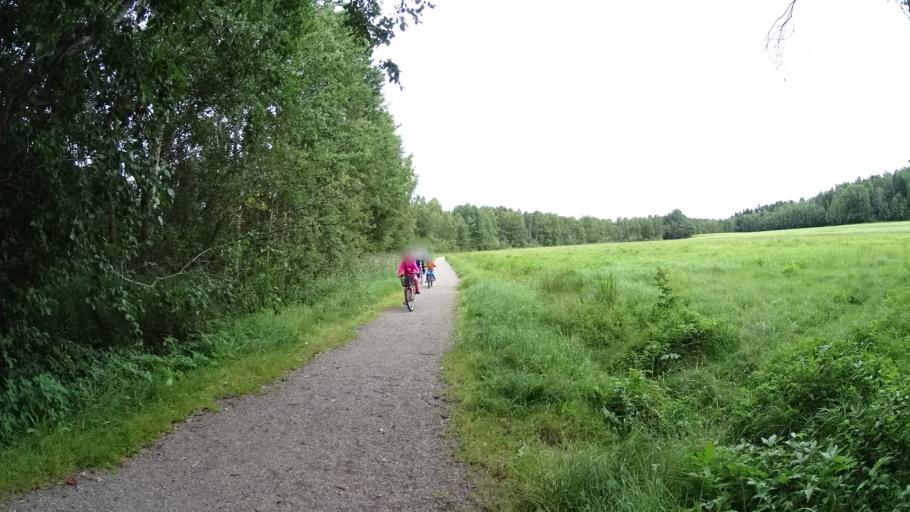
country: FI
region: Uusimaa
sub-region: Helsinki
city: Teekkarikylae
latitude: 60.2706
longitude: 24.8619
